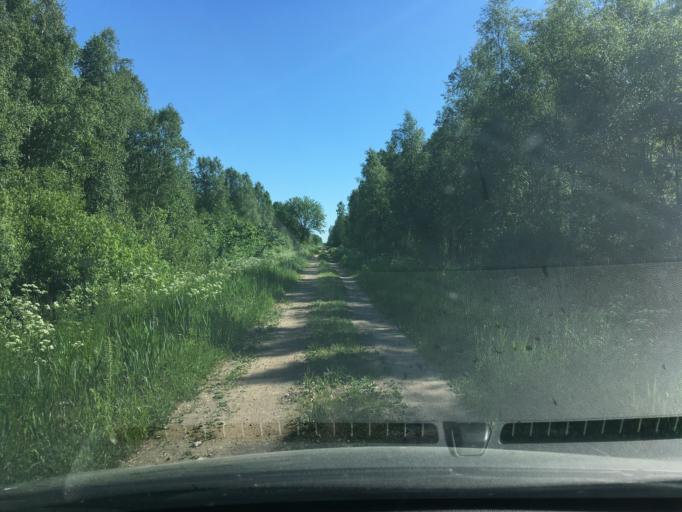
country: EE
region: Laeaene
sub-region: Lihula vald
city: Lihula
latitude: 58.6305
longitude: 23.7401
